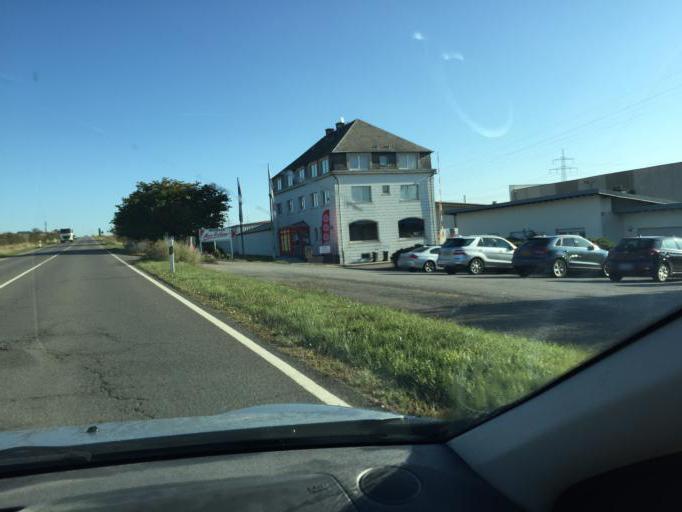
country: LU
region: Luxembourg
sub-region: Canton de Mersch
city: Bissen
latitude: 49.7814
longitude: 6.0900
